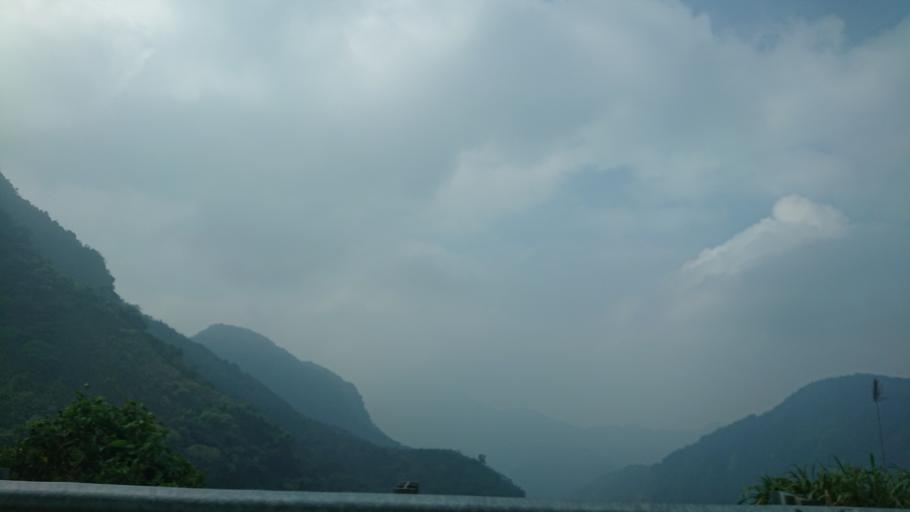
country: TW
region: Taiwan
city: Lugu
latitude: 23.5986
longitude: 120.6899
